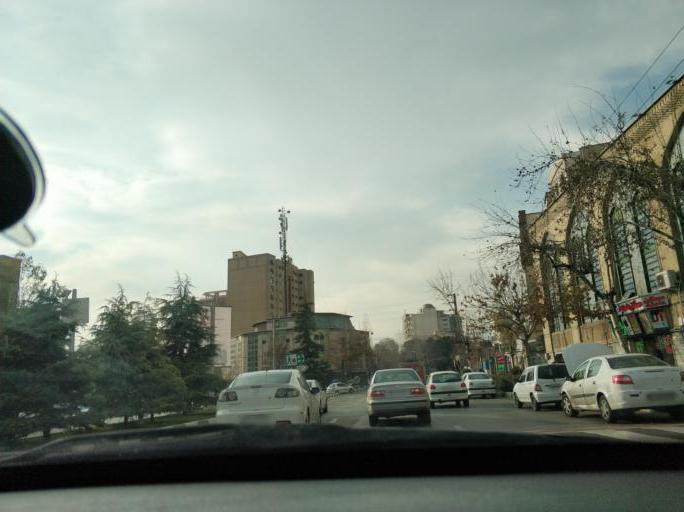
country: IR
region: Tehran
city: Tajrish
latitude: 35.8007
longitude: 51.4829
